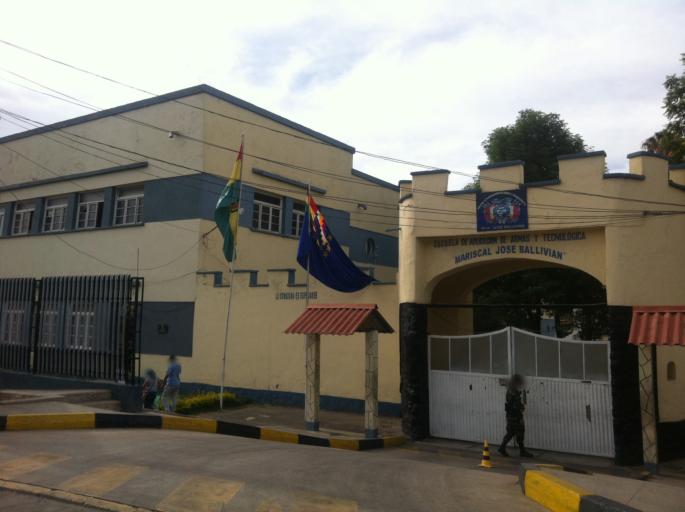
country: BO
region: Cochabamba
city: Cochabamba
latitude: -17.3790
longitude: -66.1430
